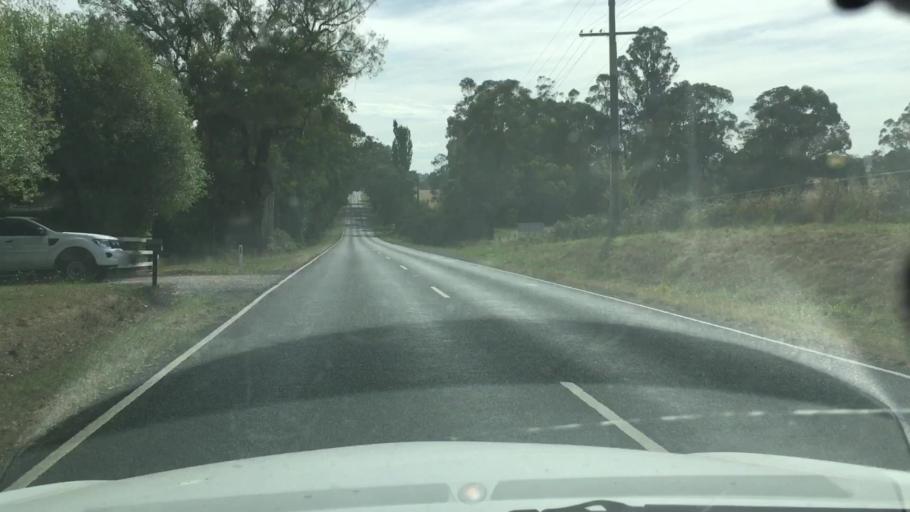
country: AU
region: Victoria
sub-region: Yarra Ranges
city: Woori Yallock
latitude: -37.8082
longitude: 145.5132
